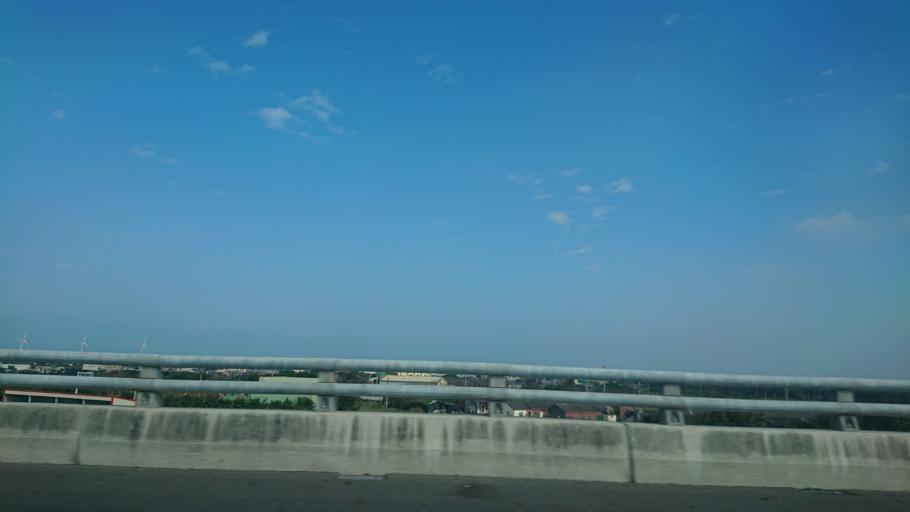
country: TW
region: Taiwan
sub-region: Changhua
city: Chang-hua
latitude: 23.9706
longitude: 120.3515
